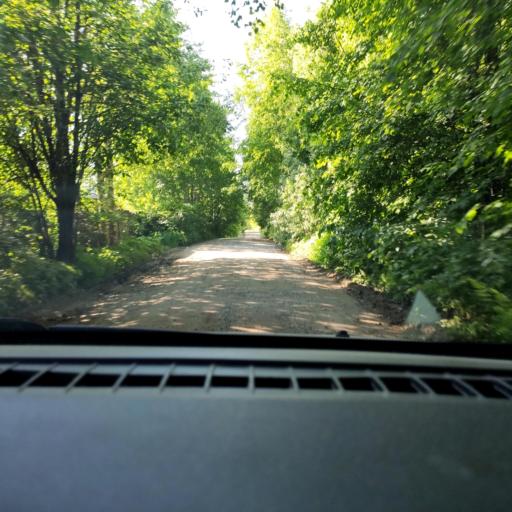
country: RU
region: Perm
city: Overyata
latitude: 58.1234
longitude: 55.8797
